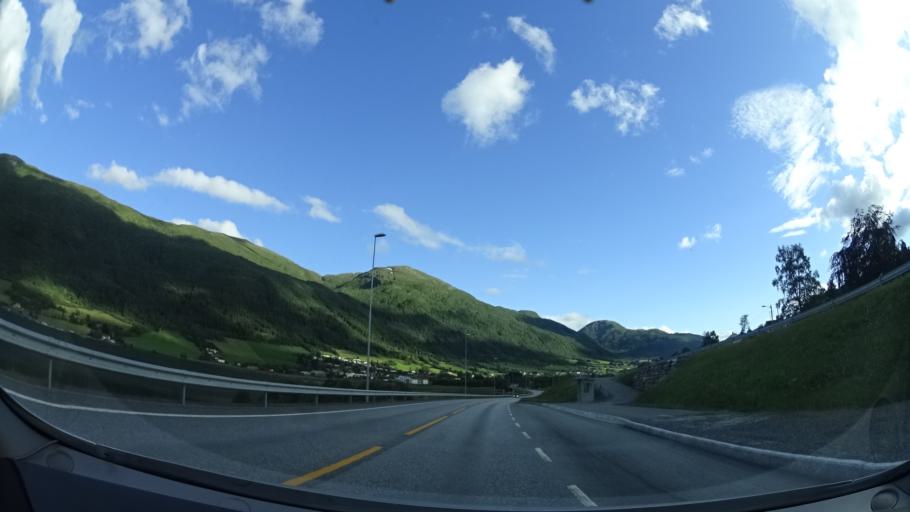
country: NO
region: More og Romsdal
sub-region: Gjemnes
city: Batnfjordsora
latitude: 62.9007
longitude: 7.6762
